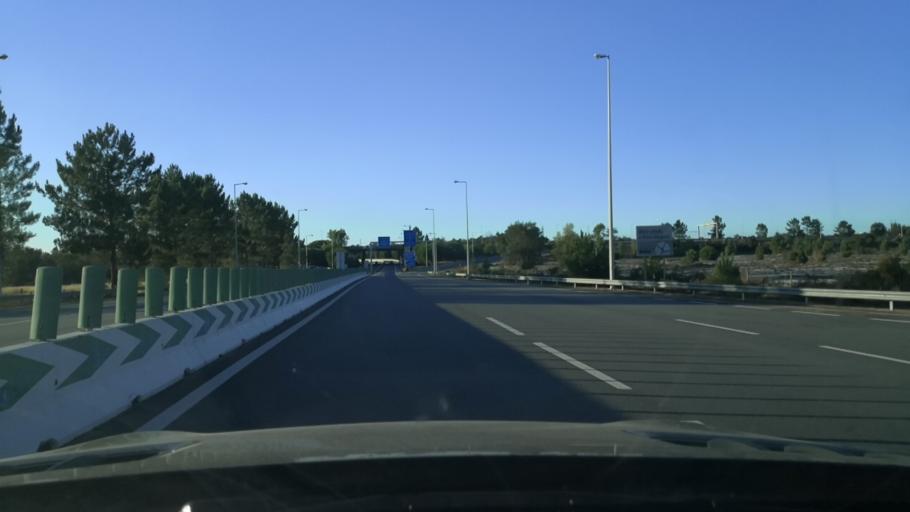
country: PT
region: Setubal
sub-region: Setubal
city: Setubal
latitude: 38.5983
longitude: -8.6736
